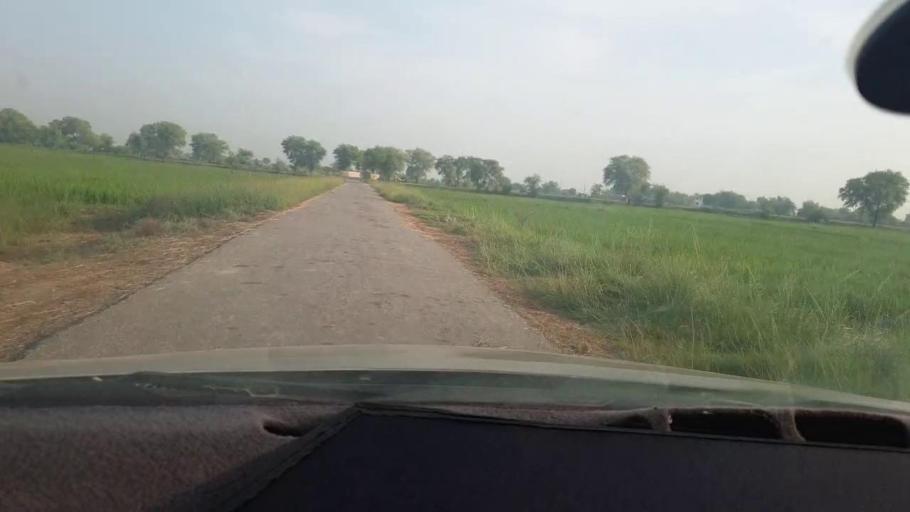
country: PK
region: Sindh
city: Jacobabad
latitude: 28.3074
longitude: 68.4144
